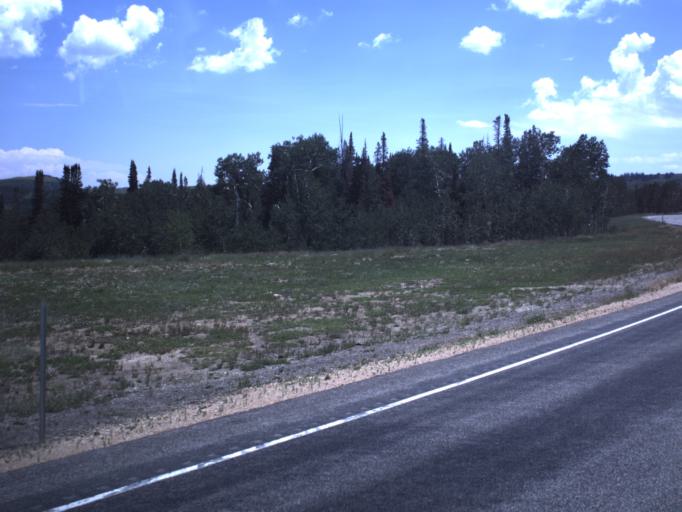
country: US
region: Utah
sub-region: Sanpete County
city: Fairview
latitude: 39.6359
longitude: -111.3291
